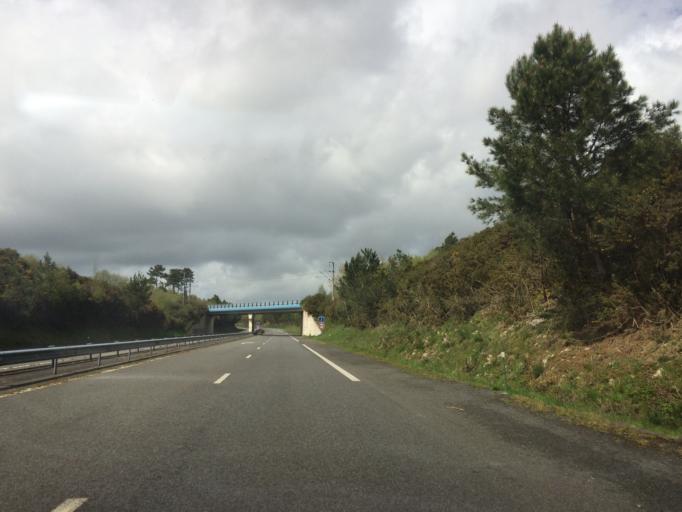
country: FR
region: Brittany
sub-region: Departement du Morbihan
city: Pluherlin
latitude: 47.6719
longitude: -2.3618
